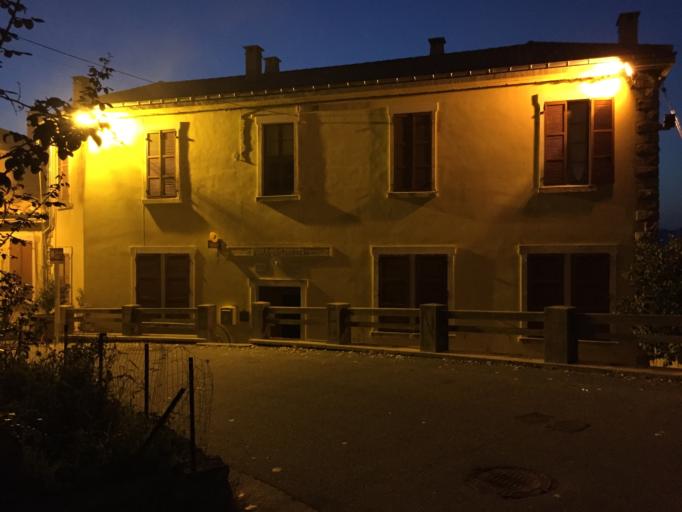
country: FR
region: Corsica
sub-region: Departement de la Corse-du-Sud
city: Cuttoli-Corticchiato
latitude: 41.9881
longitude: 8.9067
